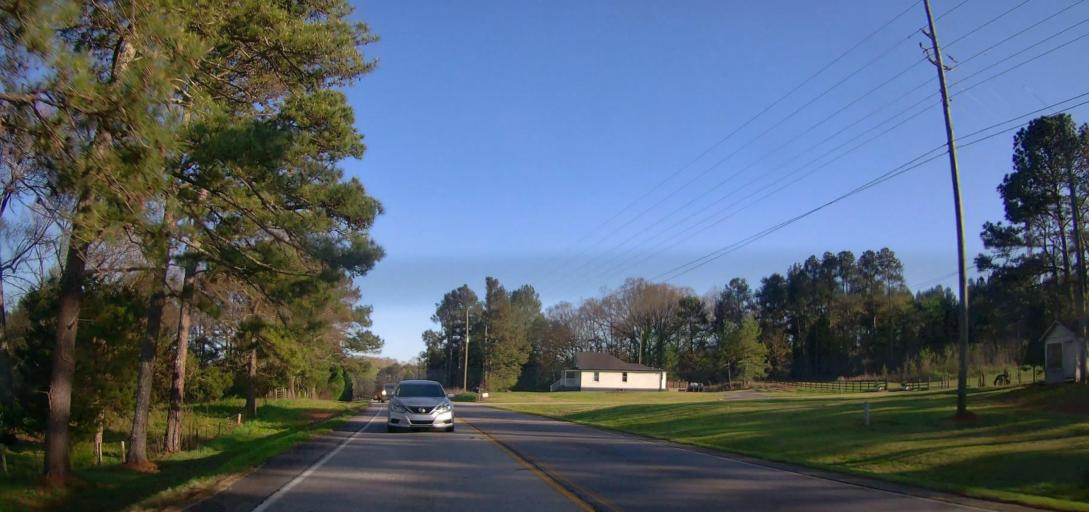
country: US
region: Georgia
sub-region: Newton County
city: Oakwood
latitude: 33.4404
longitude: -83.9008
